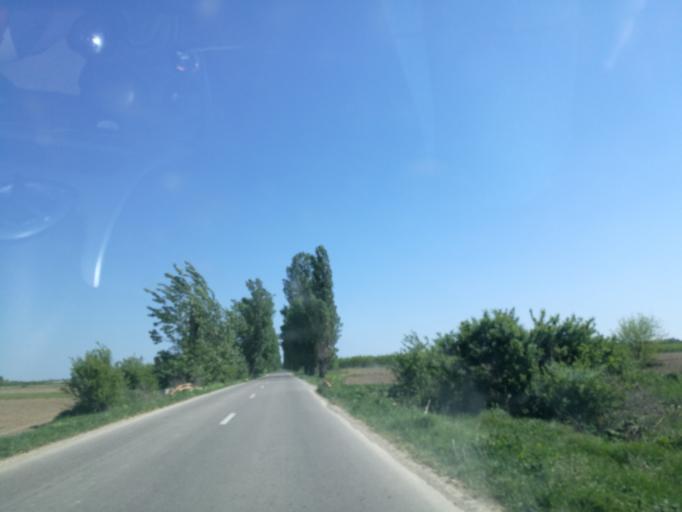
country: RO
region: Ialomita
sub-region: Comuna Maia
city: Maia
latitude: 44.7483
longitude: 26.4171
